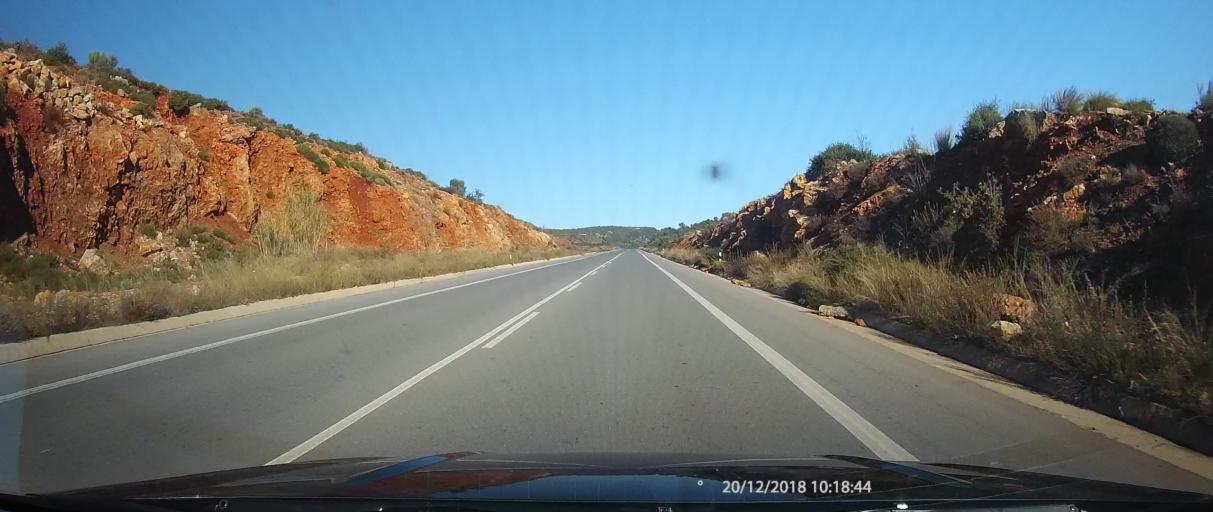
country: GR
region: Peloponnese
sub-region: Nomos Lakonias
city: Magoula
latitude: 37.1215
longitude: 22.4207
